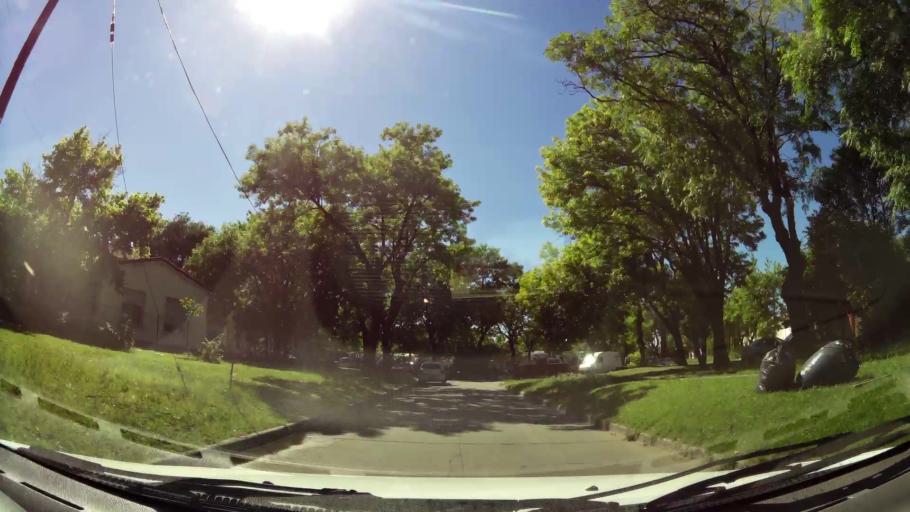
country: AR
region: Buenos Aires
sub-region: Partido de General San Martin
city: General San Martin
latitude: -34.5450
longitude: -58.5315
